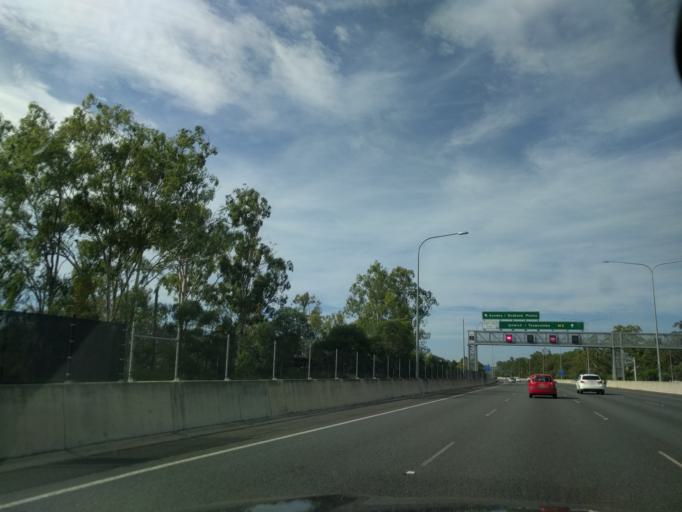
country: AU
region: Queensland
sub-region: Brisbane
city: Wacol
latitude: -27.5943
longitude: 152.9232
